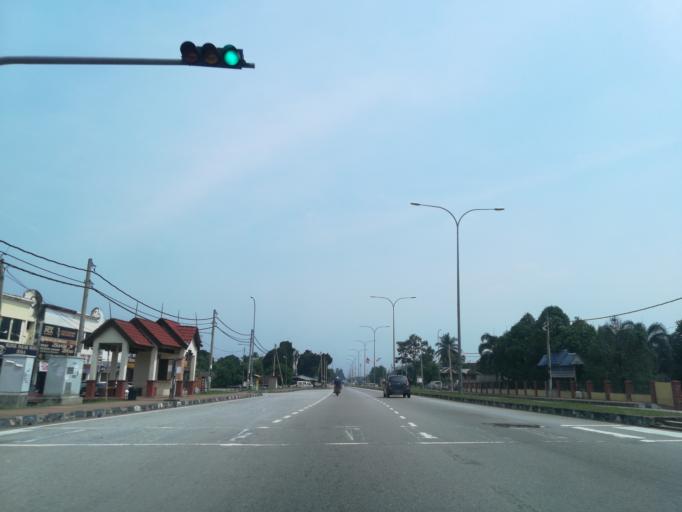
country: MY
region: Kedah
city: Kulim
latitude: 5.3948
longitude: 100.5605
